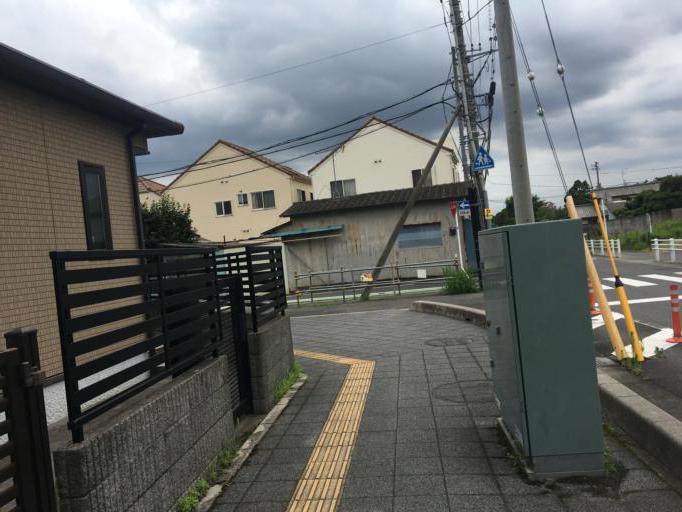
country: JP
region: Saitama
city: Kasukabe
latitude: 35.9833
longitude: 139.7504
